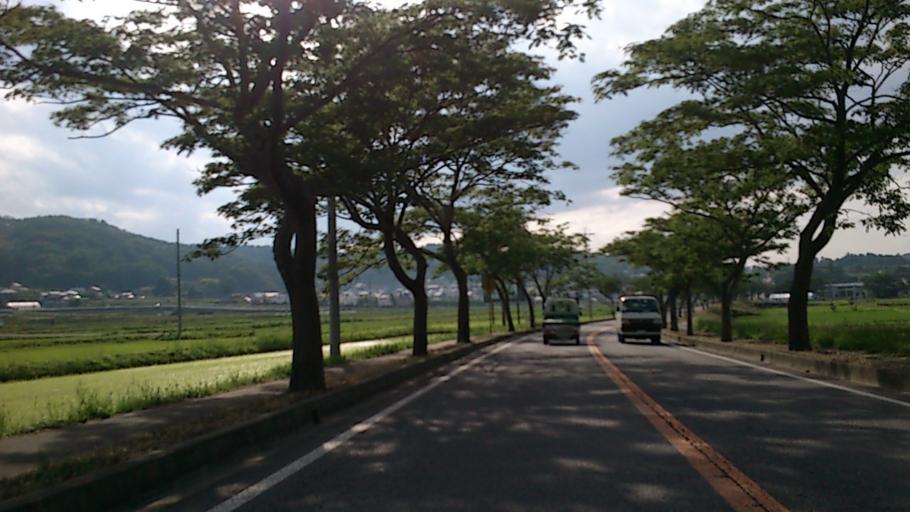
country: JP
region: Nagano
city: Saku
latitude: 36.2424
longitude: 138.4245
